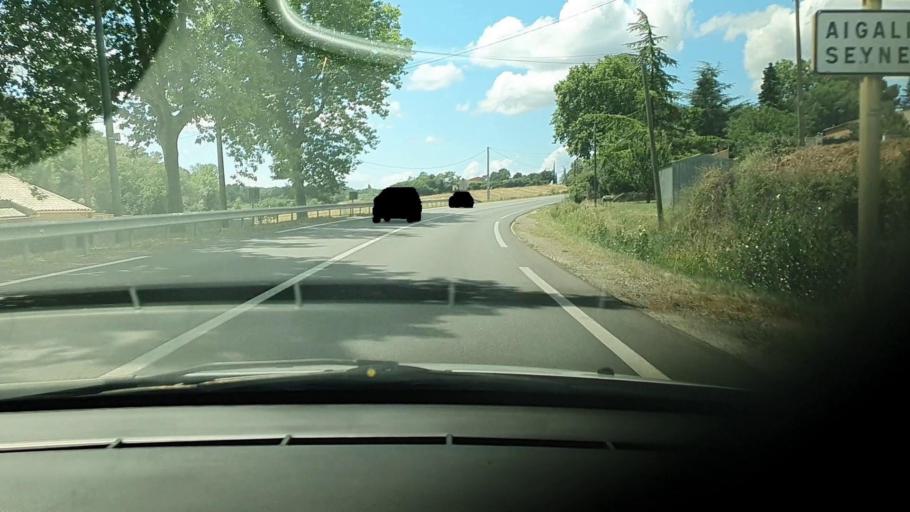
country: FR
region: Languedoc-Roussillon
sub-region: Departement du Gard
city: Montaren-et-Saint-Mediers
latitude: 44.0391
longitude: 4.3541
